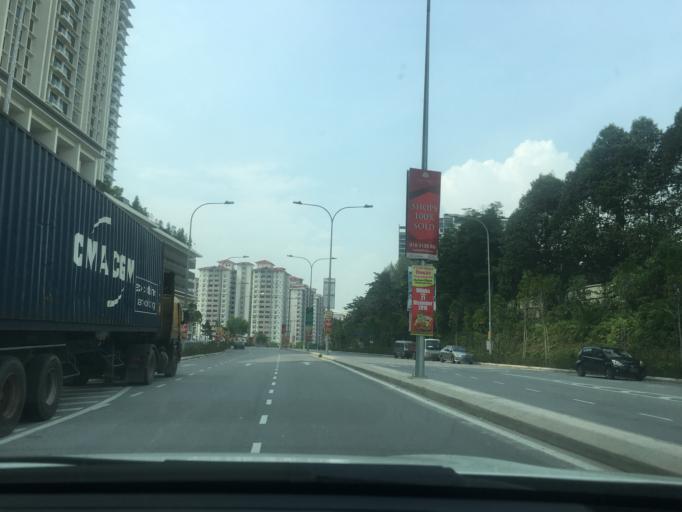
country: MY
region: Selangor
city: Kampong Baharu Balakong
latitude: 3.0529
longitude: 101.6729
